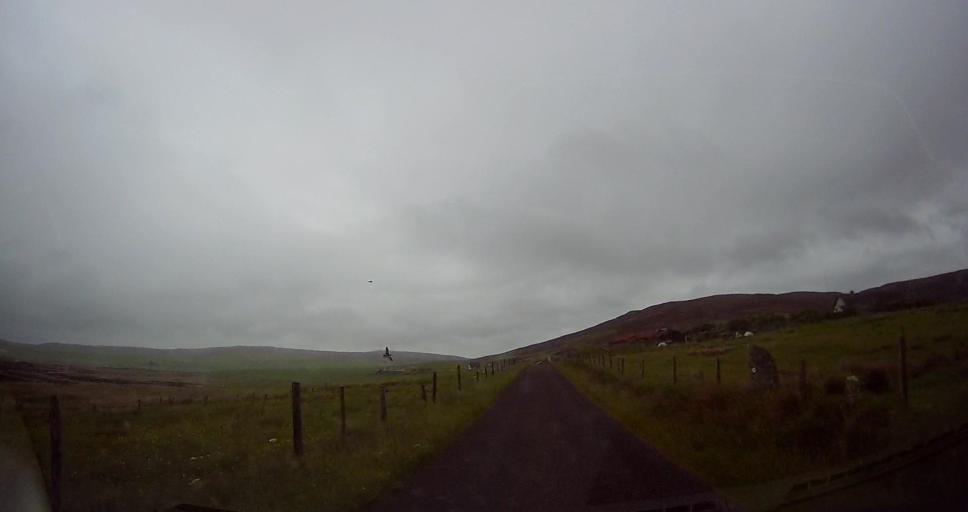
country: GB
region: Scotland
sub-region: Orkney Islands
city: Stromness
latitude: 58.9780
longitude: -3.1699
